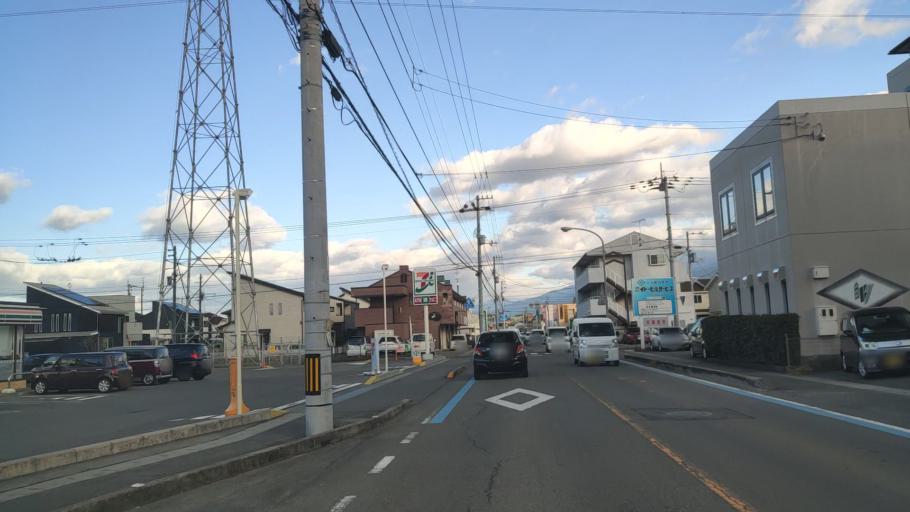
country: JP
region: Ehime
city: Saijo
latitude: 33.9152
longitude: 133.1691
